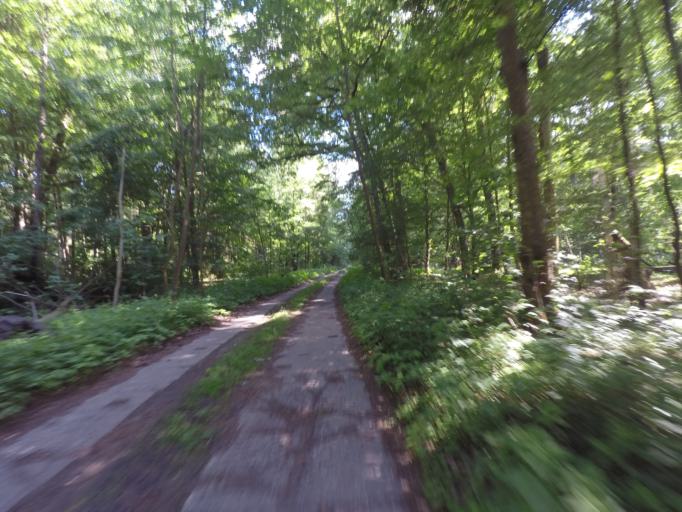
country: DE
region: Brandenburg
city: Britz
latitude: 52.8648
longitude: 13.7845
